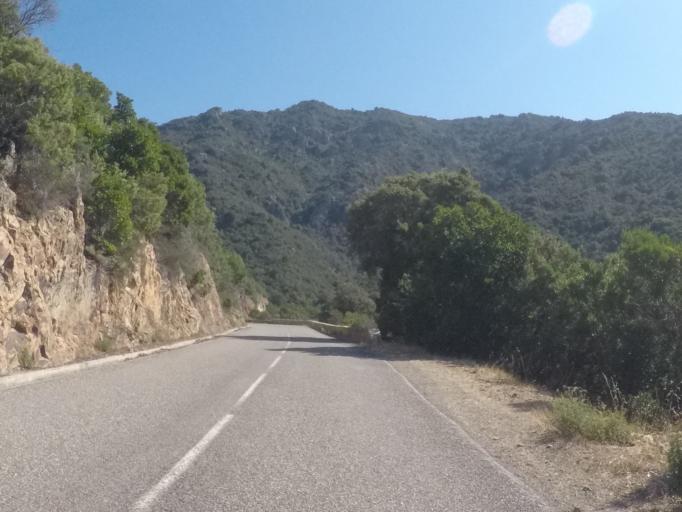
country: FR
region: Corsica
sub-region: Departement de la Haute-Corse
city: Calvi
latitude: 42.3713
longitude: 8.6695
